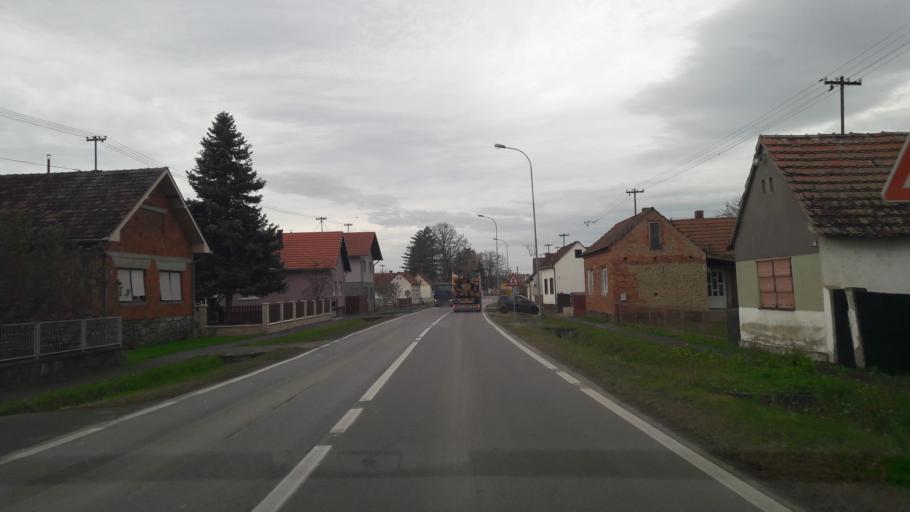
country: HR
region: Virovitick-Podravska
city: Orahovica
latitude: 45.5473
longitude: 17.9053
